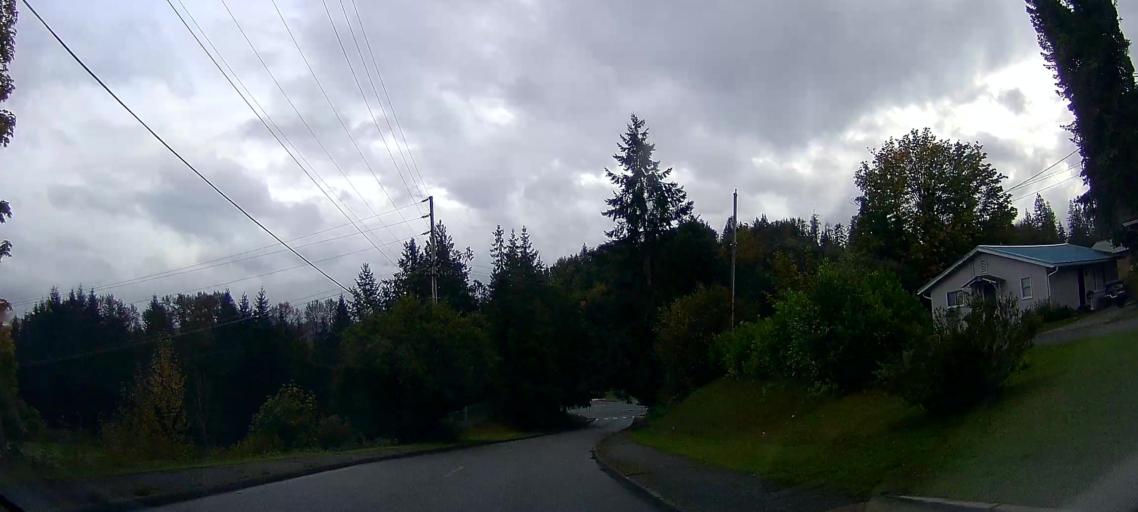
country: US
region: Washington
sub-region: Snohomish County
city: Darrington
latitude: 48.5386
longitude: -121.7448
